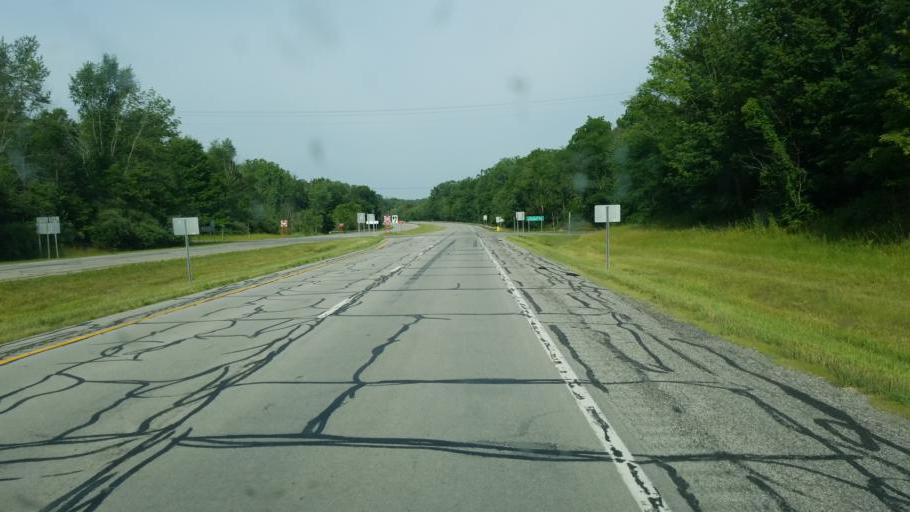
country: US
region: Ohio
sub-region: Medina County
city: Lodi
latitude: 41.0449
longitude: -82.0332
